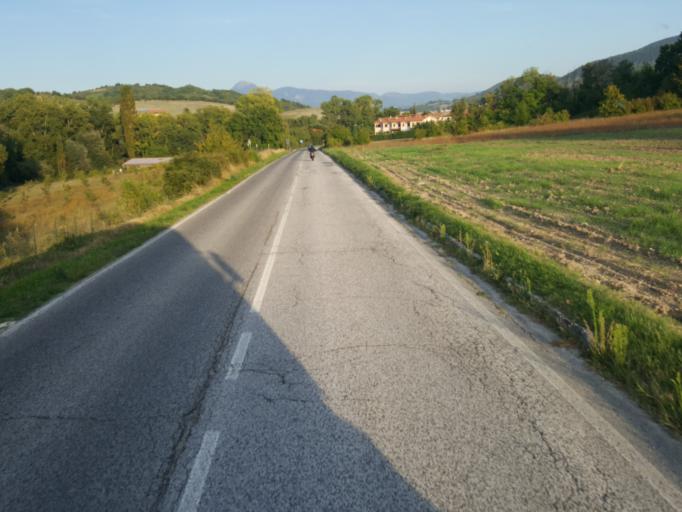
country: IT
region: The Marches
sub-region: Provincia di Ancona
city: Fabriano
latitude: 43.3502
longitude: 12.8326
